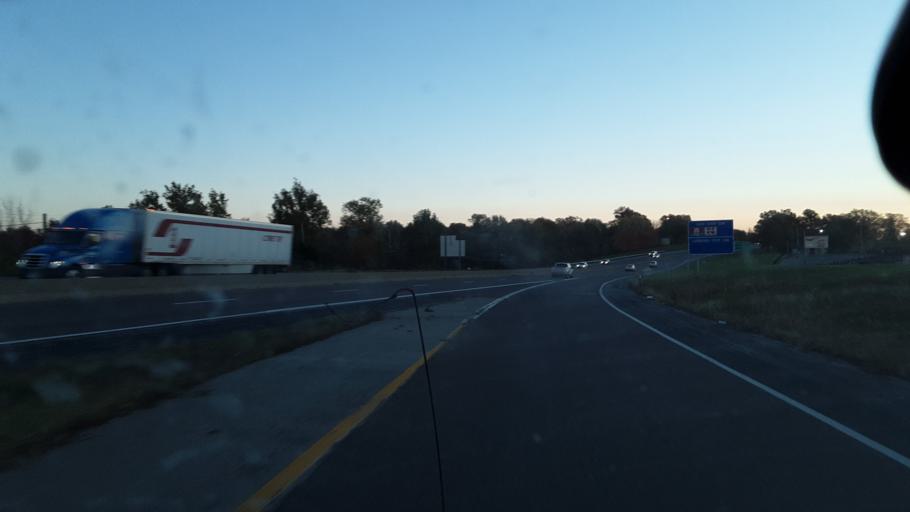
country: US
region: Missouri
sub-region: Boone County
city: Columbia
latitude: 38.9683
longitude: -92.3481
